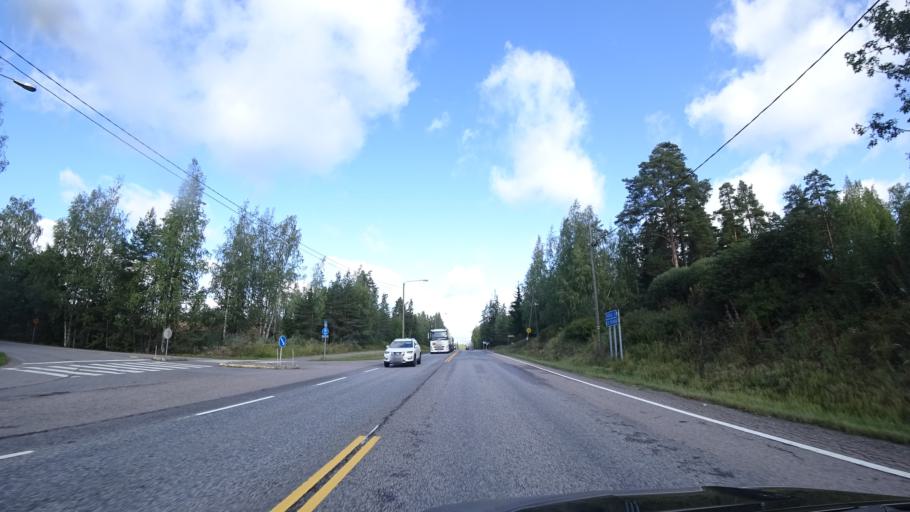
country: FI
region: Uusimaa
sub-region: Helsinki
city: Tuusula
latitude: 60.4389
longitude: 24.9801
